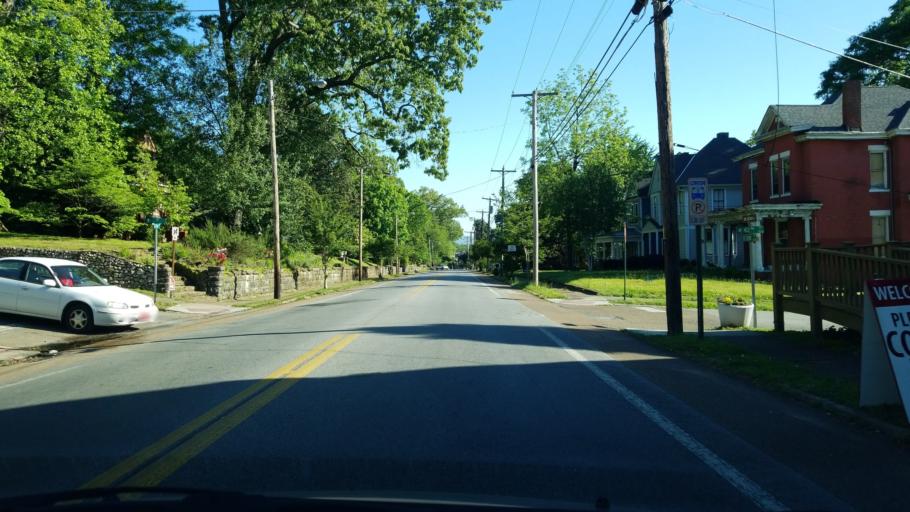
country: US
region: Tennessee
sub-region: Hamilton County
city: Lookout Mountain
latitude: 35.0046
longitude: -85.3289
